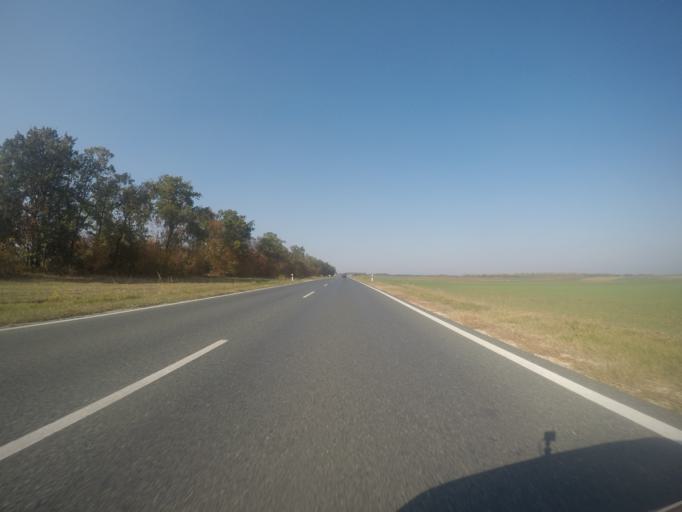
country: HU
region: Tolna
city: Madocsa
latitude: 46.7204
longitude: 18.8853
